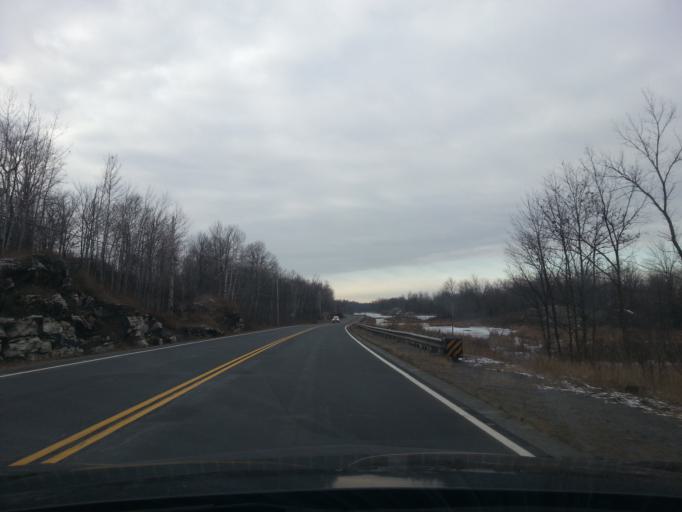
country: CA
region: Ontario
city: Deseronto
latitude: 44.5896
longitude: -77.1924
